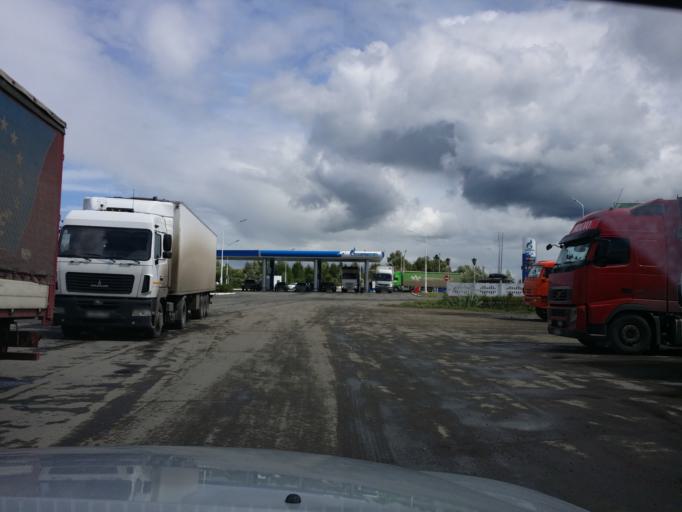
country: RU
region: Tjumen
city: Tobol'sk
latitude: 58.2997
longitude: 68.3127
